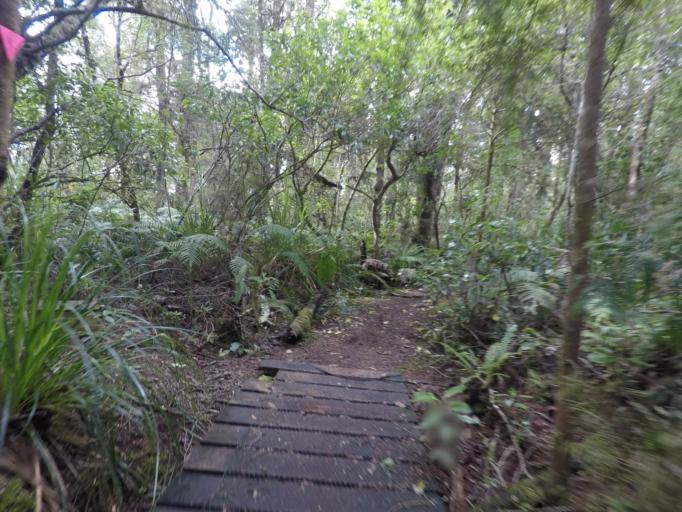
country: NZ
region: Manawatu-Wanganui
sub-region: Ruapehu District
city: Waiouru
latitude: -39.4187
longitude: 175.3940
